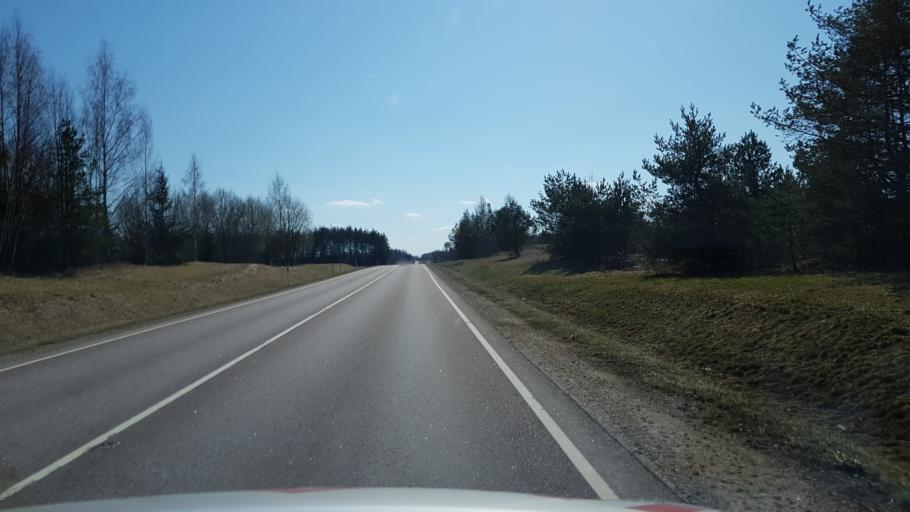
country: EE
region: Jogevamaa
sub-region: Mustvee linn
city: Mustvee
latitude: 58.7268
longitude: 26.8368
